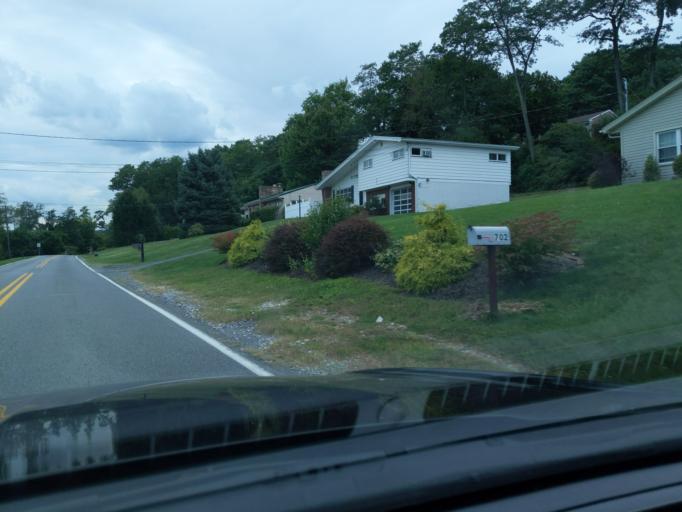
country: US
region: Pennsylvania
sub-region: Blair County
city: Lakemont
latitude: 40.4736
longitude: -78.4124
